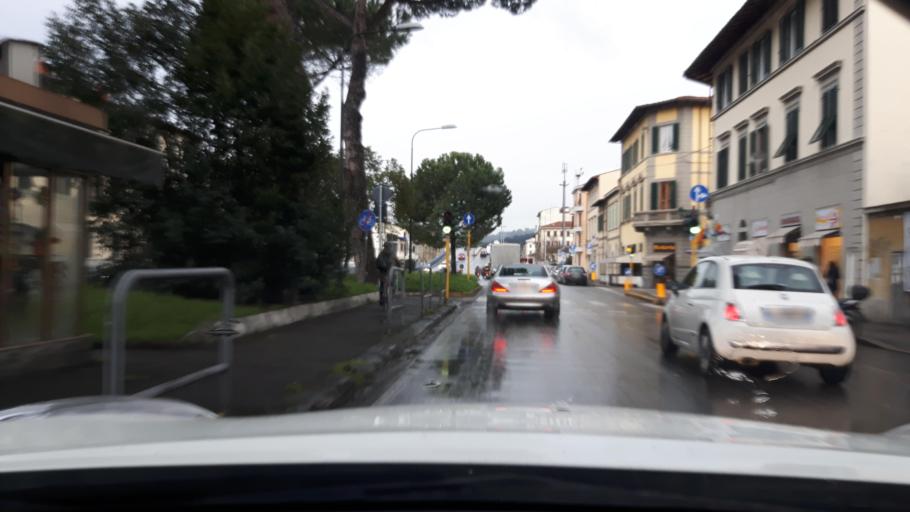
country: IT
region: Tuscany
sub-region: Province of Florence
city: Fiesole
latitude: 43.7730
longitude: 11.2847
